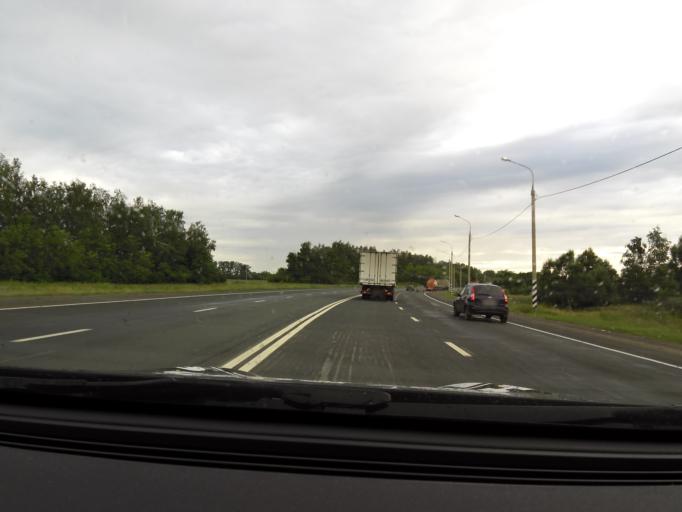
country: RU
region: Chuvashia
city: Yantikovo
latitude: 55.7961
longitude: 48.0657
